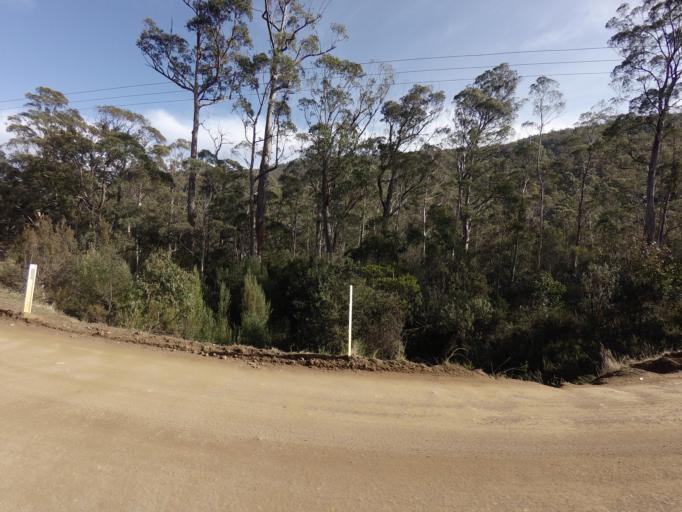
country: AU
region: Tasmania
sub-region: Huon Valley
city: Huonville
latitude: -43.0557
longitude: 147.0991
